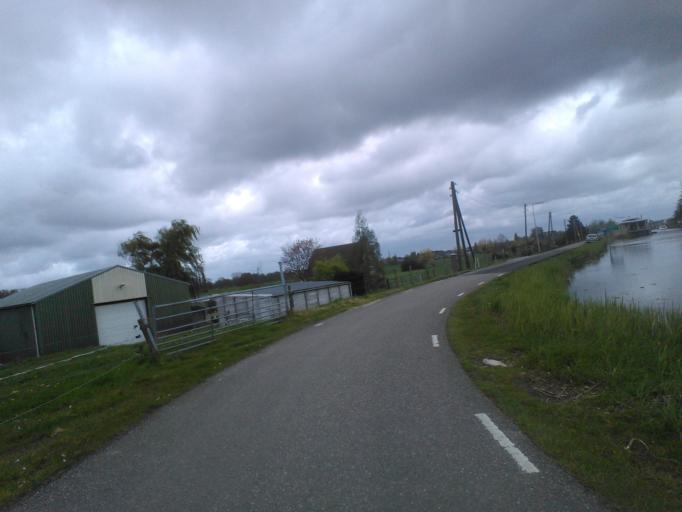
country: NL
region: South Holland
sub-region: Gemeente Gouda
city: Bloemendaal
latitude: 51.9793
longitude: 4.6523
